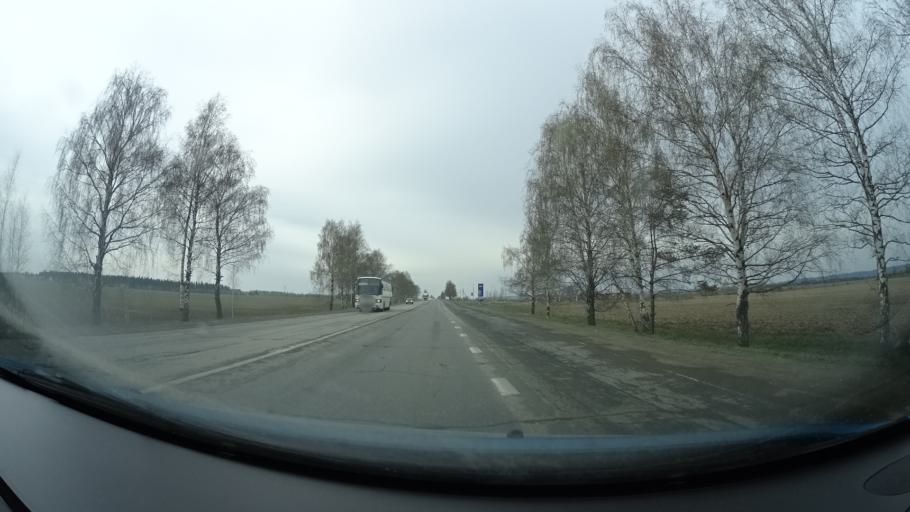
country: RU
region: Perm
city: Ust'-Kachka
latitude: 58.0717
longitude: 55.6341
